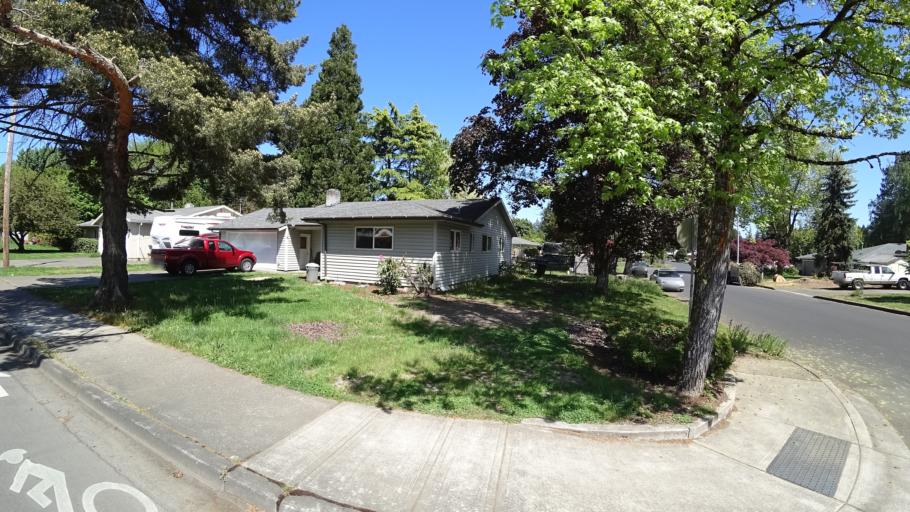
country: US
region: Oregon
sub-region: Washington County
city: Hillsboro
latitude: 45.5132
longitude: -122.9496
